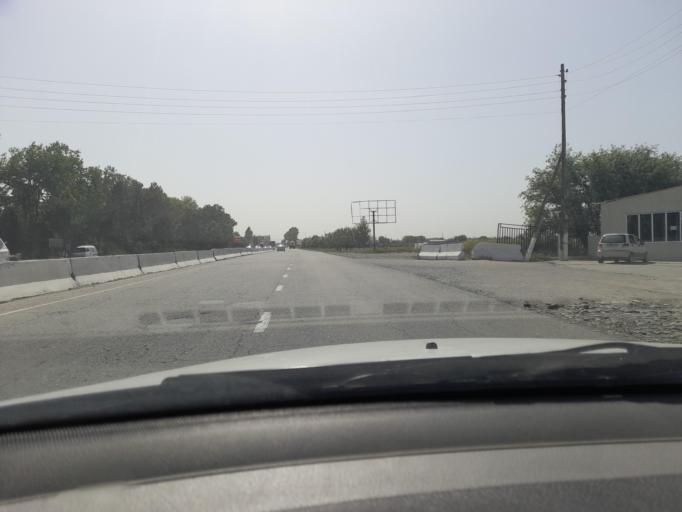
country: UZ
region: Samarqand
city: Jomboy
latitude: 39.7198
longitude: 67.1186
